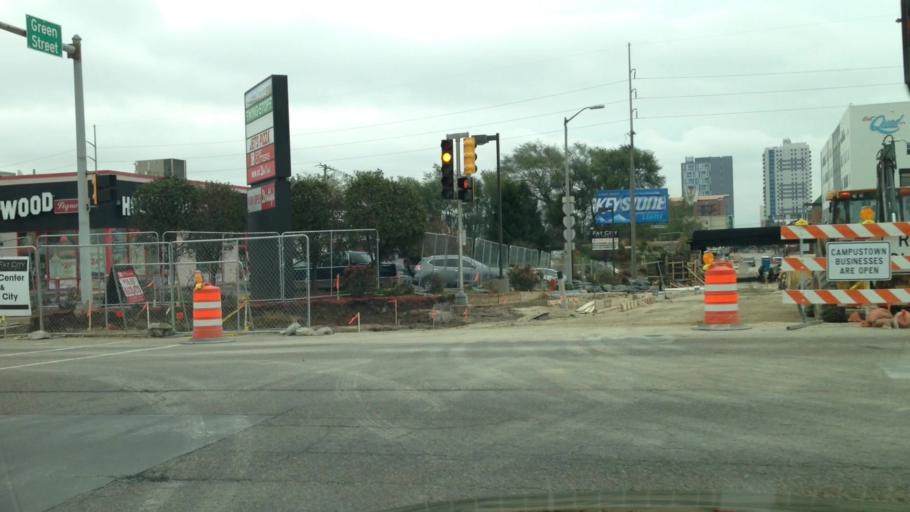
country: US
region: Illinois
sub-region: Champaign County
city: Champaign
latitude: 40.1102
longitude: -88.2436
